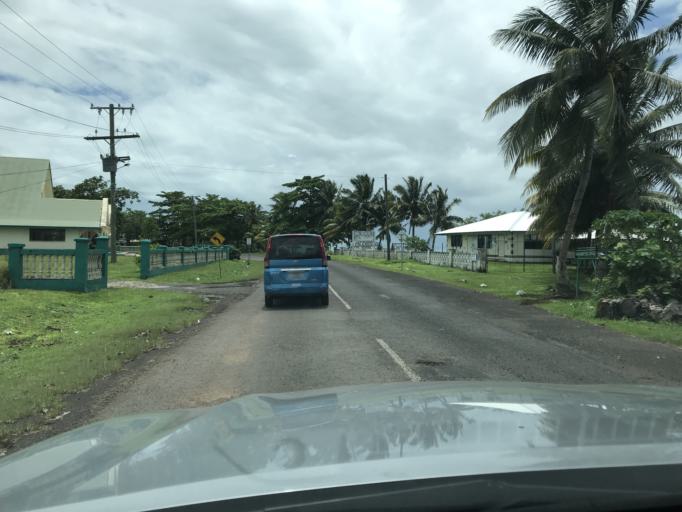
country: WS
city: Fasito`outa
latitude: -13.8069
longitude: -171.9279
